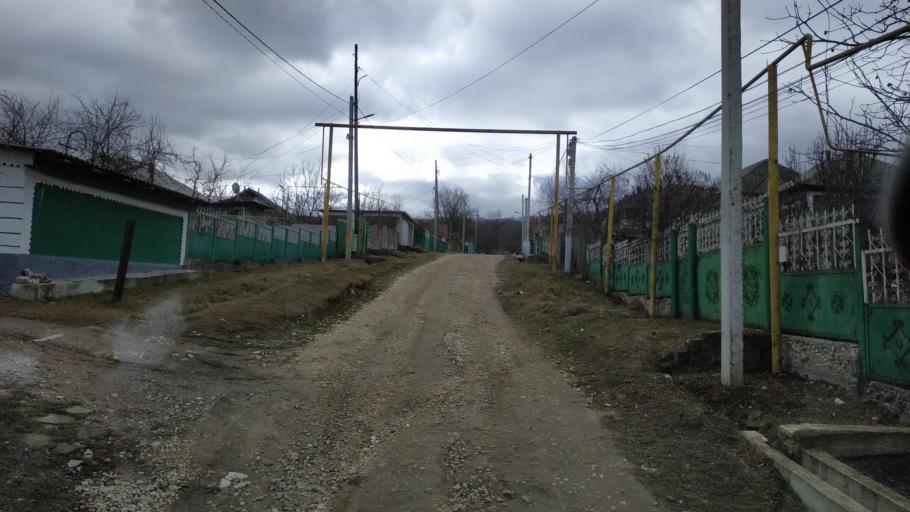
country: MD
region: Calarasi
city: Calarasi
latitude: 47.2363
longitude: 28.3103
